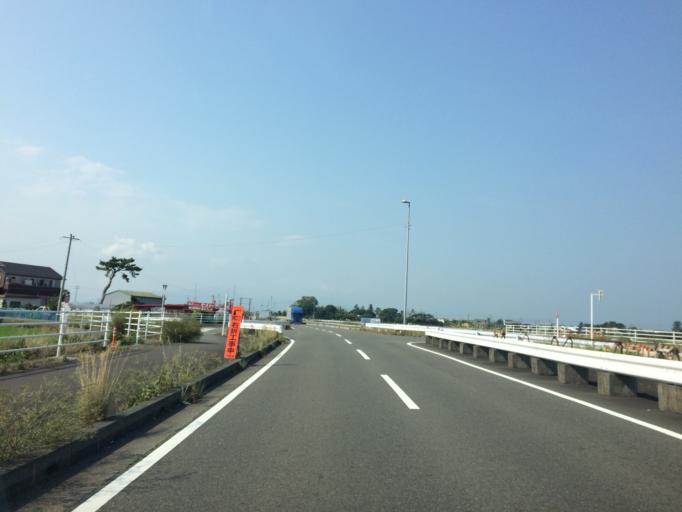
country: JP
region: Shizuoka
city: Yaizu
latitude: 34.8072
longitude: 138.3105
